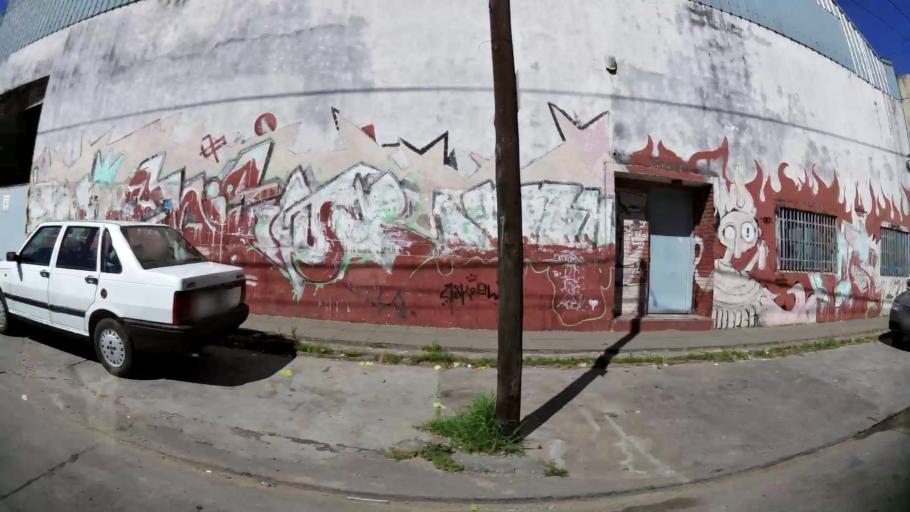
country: AR
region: Buenos Aires
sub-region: Partido de General San Martin
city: General San Martin
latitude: -34.5465
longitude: -58.5324
